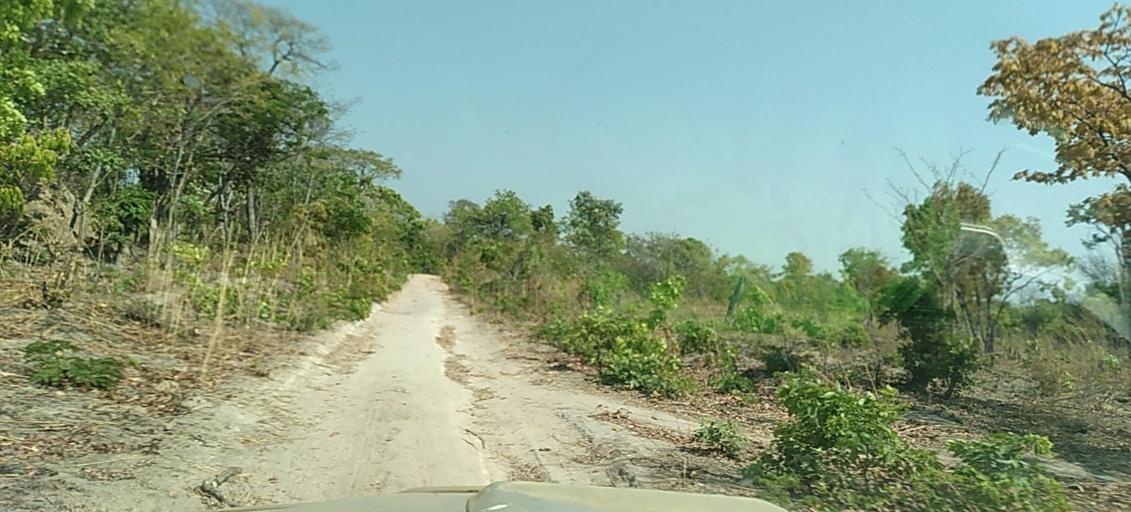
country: ZM
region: North-Western
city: Kalengwa
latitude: -13.3149
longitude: 24.8142
